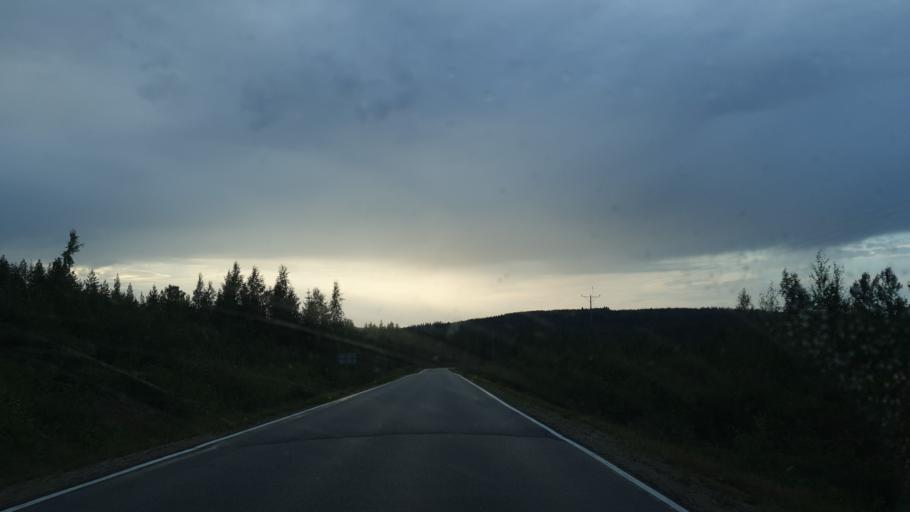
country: FI
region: North Karelia
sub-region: Pielisen Karjala
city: Lieksa
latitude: 63.6132
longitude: 29.8582
